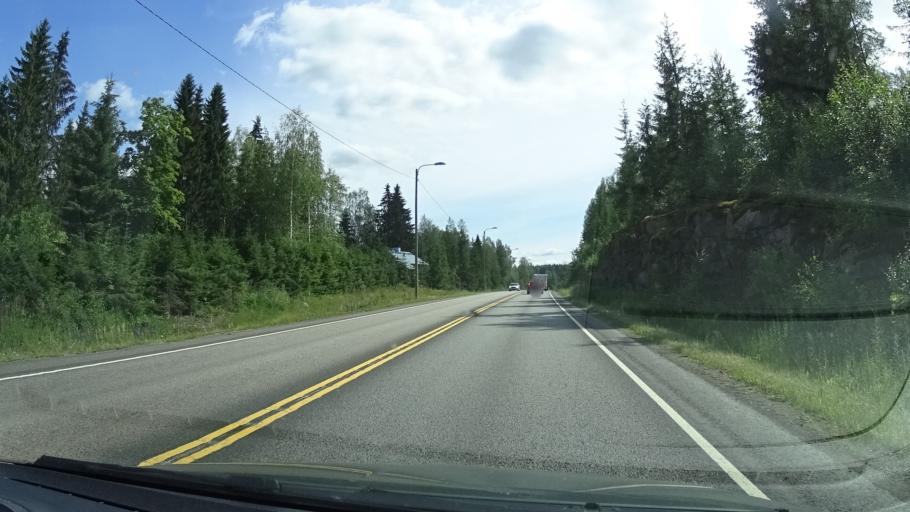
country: FI
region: Central Finland
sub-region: Jyvaeskylae
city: Jyvaeskylae
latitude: 62.2687
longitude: 25.5505
